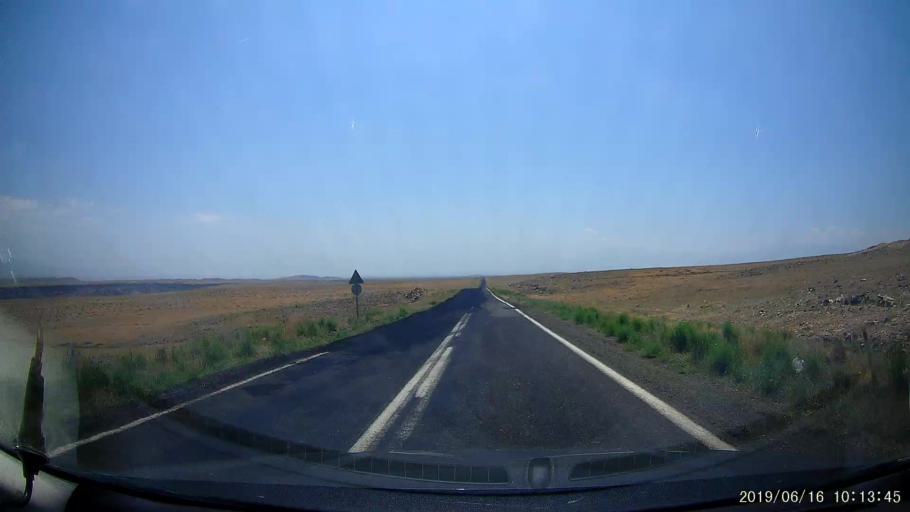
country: TR
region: Igdir
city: Tuzluca
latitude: 40.1908
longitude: 43.6486
